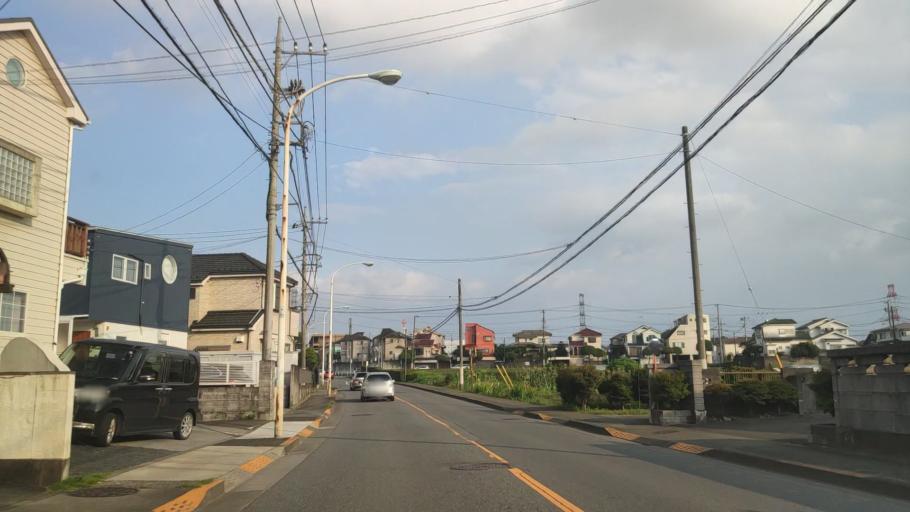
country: JP
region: Saitama
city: Hanno
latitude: 35.8027
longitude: 139.3090
